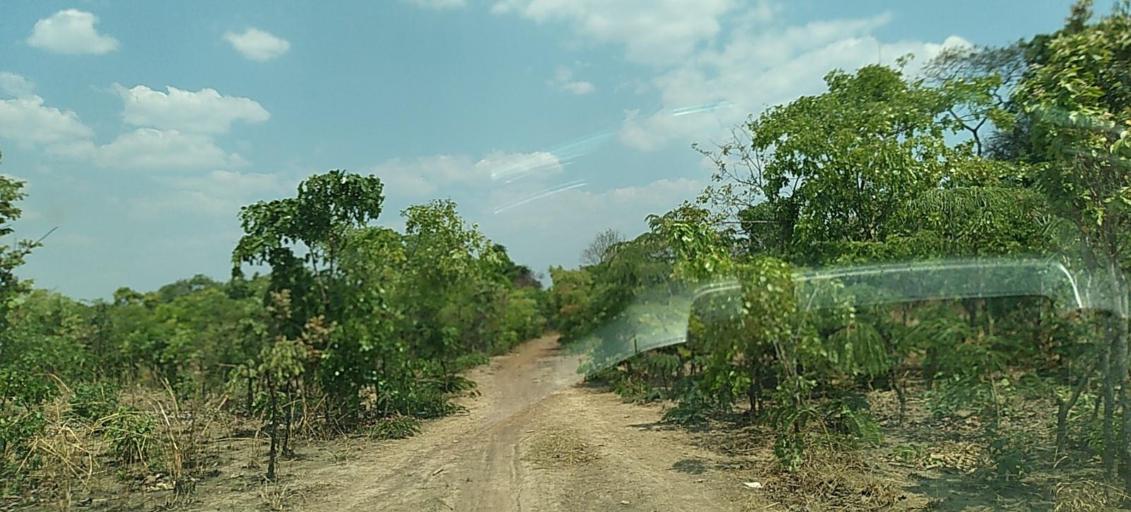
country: CD
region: Katanga
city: Kipushi
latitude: -11.9993
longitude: 27.4223
